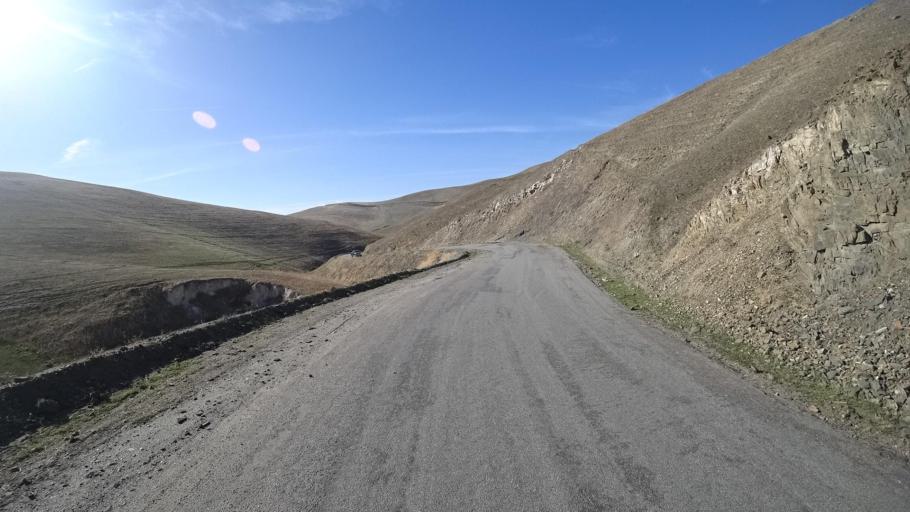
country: US
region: California
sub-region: Kern County
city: Arvin
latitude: 35.4084
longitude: -118.7662
